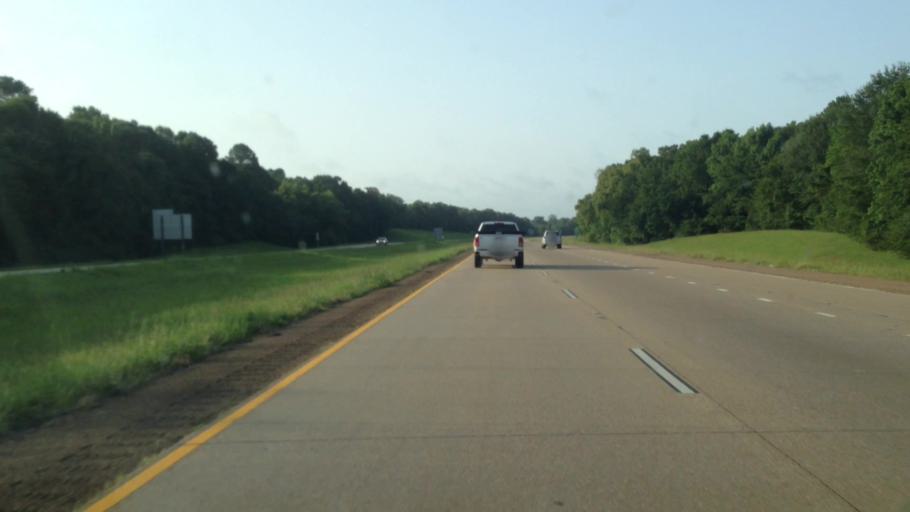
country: US
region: Louisiana
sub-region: Rapides Parish
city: Woodworth
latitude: 31.1588
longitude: -92.4567
